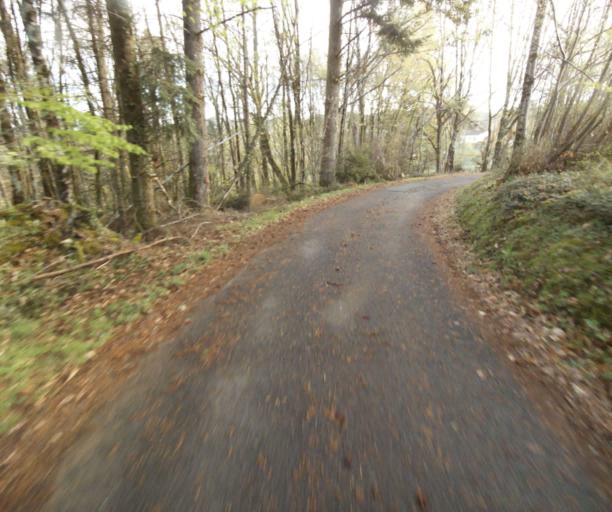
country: FR
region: Limousin
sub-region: Departement de la Correze
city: Naves
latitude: 45.3113
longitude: 1.8235
